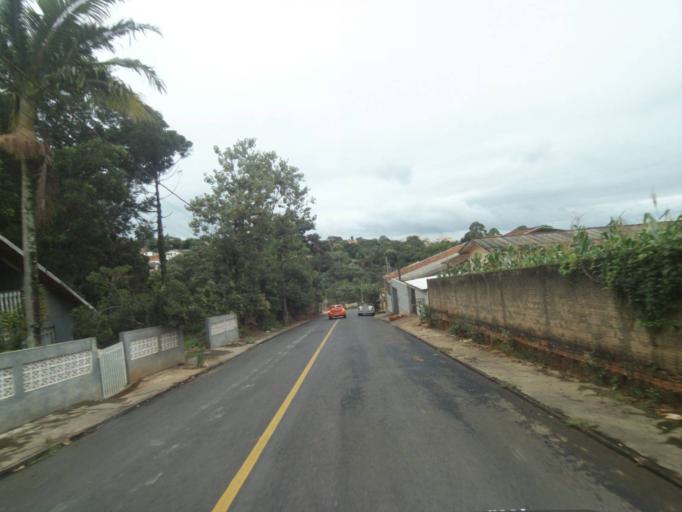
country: BR
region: Parana
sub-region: Telemaco Borba
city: Telemaco Borba
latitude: -24.3272
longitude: -50.6461
